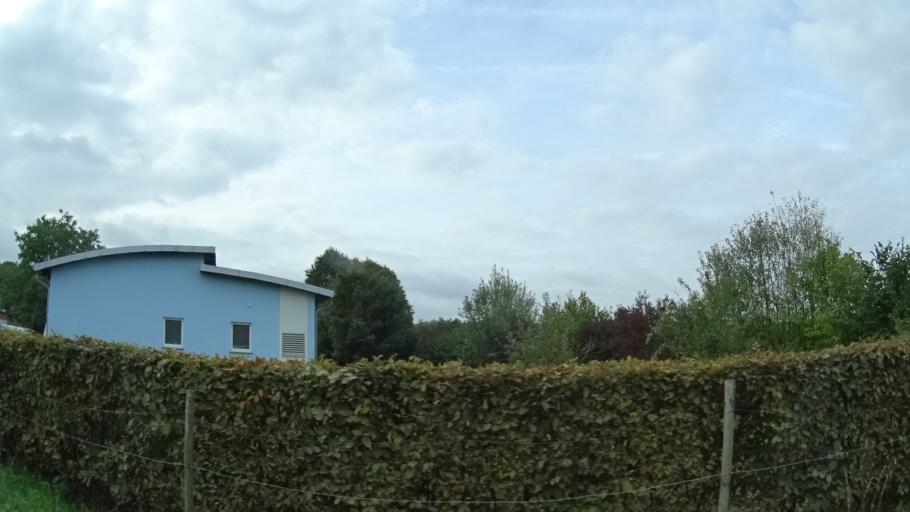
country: DE
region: Hesse
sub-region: Regierungsbezirk Kassel
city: Hofbieber
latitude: 50.5738
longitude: 9.8326
